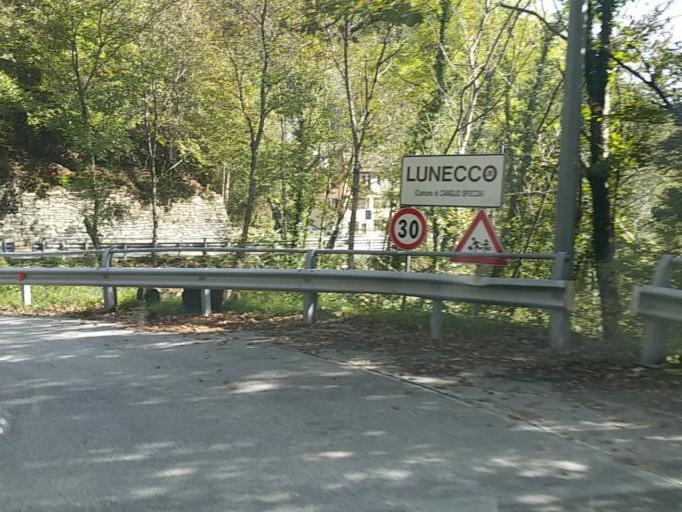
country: IT
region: Piedmont
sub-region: Provincia Verbano-Cusio-Ossola
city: Falmenta
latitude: 46.0717
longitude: 8.6052
